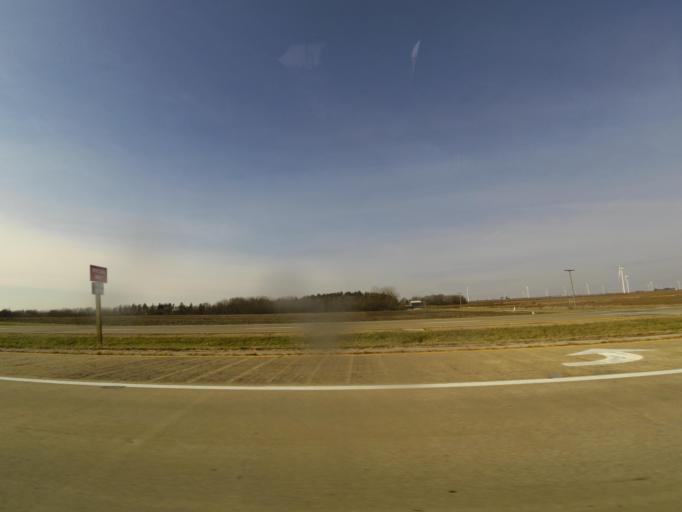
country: US
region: Illinois
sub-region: Macon County
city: Forsyth
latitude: 39.9636
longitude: -88.9559
